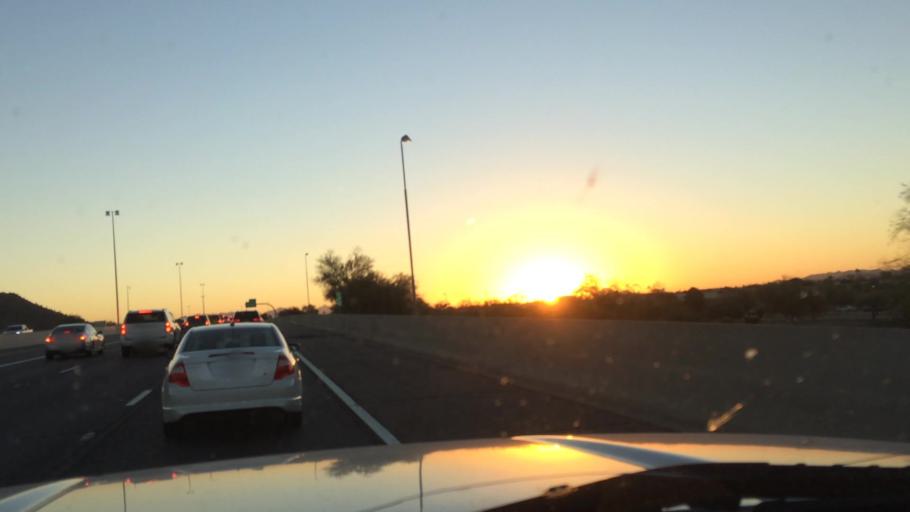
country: US
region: Arizona
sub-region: Maricopa County
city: Peoria
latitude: 33.6679
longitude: -112.1733
